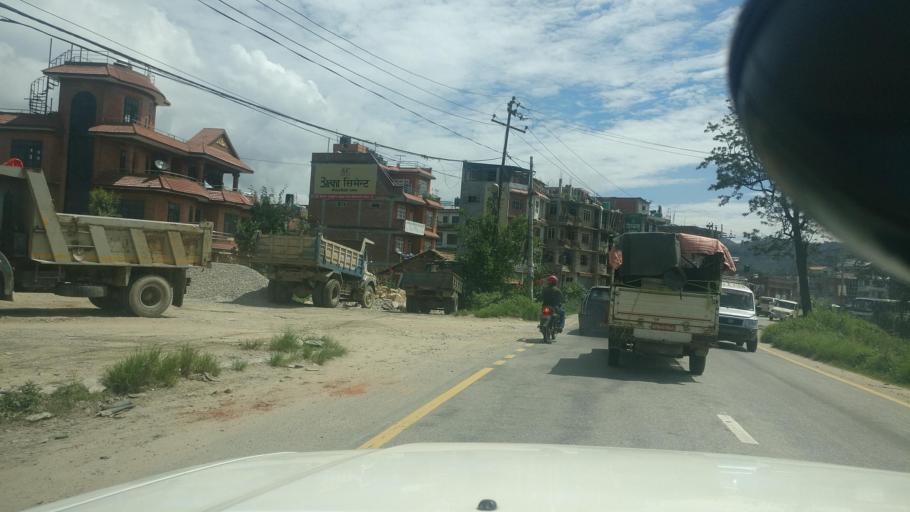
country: NP
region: Central Region
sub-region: Bagmati Zone
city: Hari Bdr Tamang House
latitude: 27.6538
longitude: 85.4589
